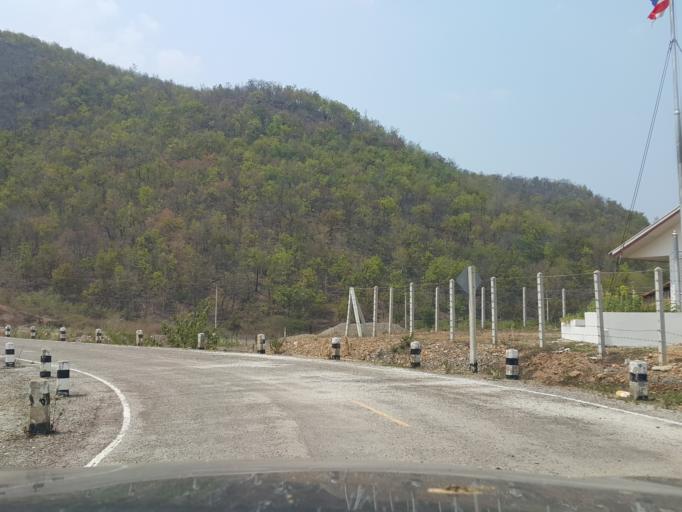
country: TH
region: Lampang
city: Mae Phrik
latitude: 17.5034
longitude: 99.0683
